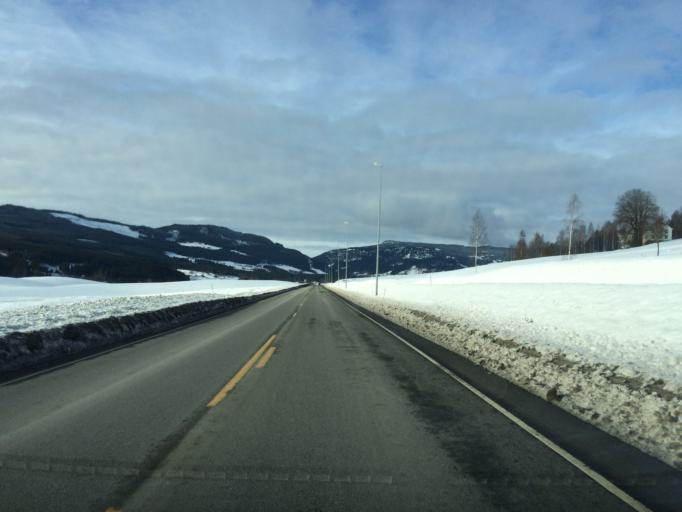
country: NO
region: Oppland
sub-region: Gausdal
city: Segalstad bru
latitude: 61.2204
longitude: 10.2653
